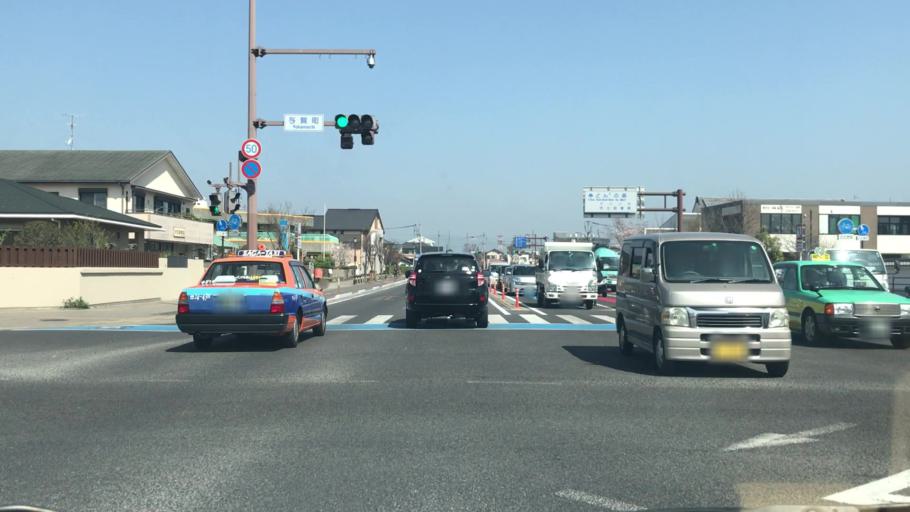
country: JP
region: Saga Prefecture
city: Saga-shi
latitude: 33.2500
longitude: 130.2924
